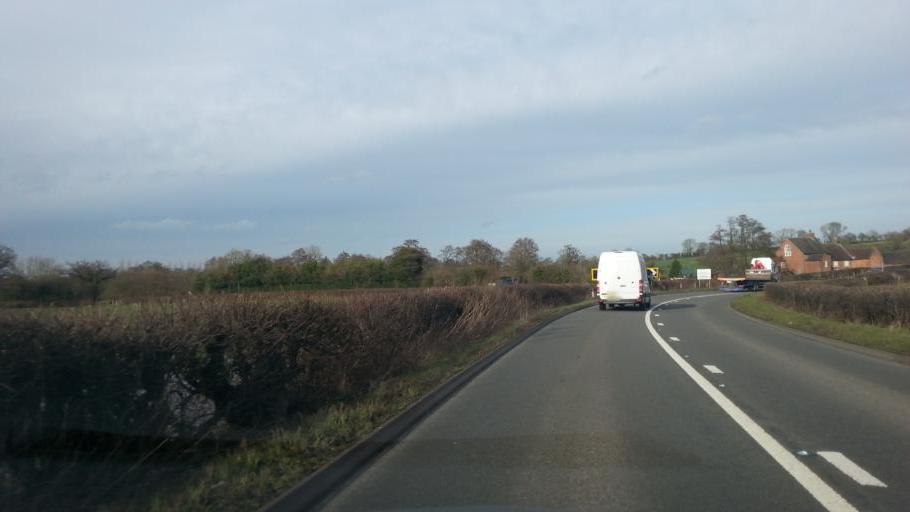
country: GB
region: England
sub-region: Staffordshire
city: Uttoxeter
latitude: 52.8765
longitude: -1.9376
